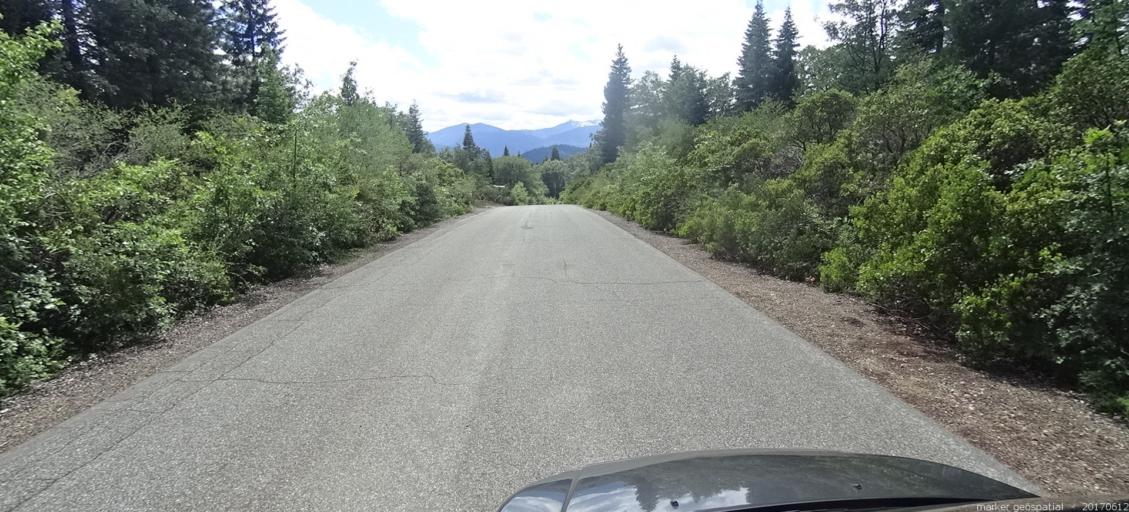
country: US
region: California
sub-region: Siskiyou County
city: Mount Shasta
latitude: 41.3042
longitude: -122.2897
